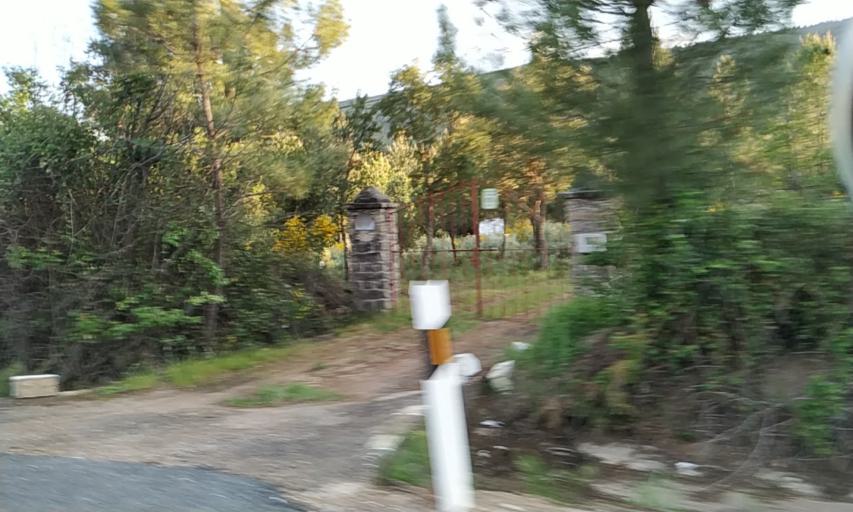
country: PT
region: Portalegre
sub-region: Portalegre
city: Sao Juliao
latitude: 39.3441
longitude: -7.2955
